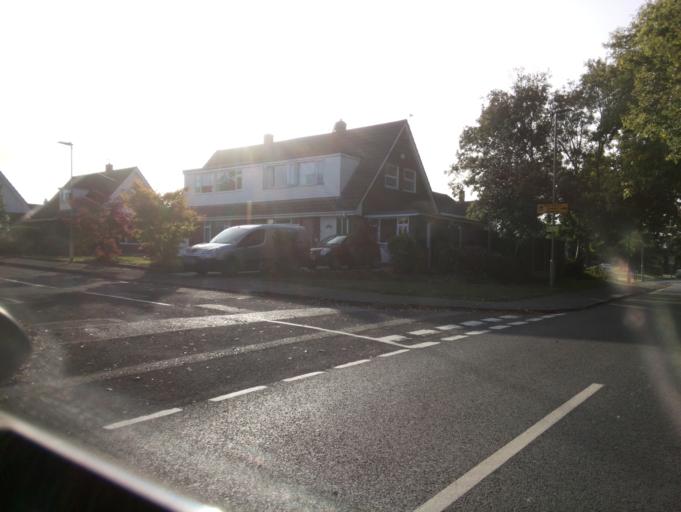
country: GB
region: England
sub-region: Gloucestershire
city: Gloucester
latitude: 51.8503
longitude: -2.2681
